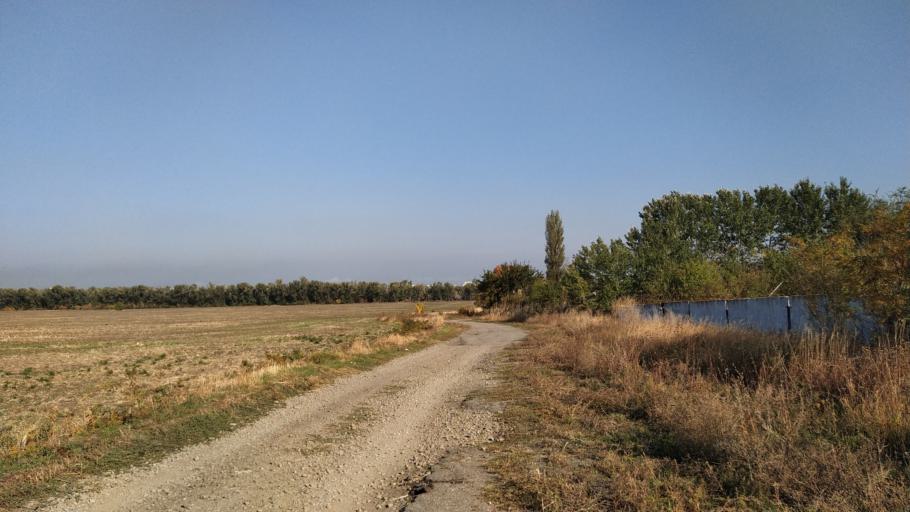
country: RU
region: Rostov
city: Bataysk
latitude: 47.0907
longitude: 39.7764
